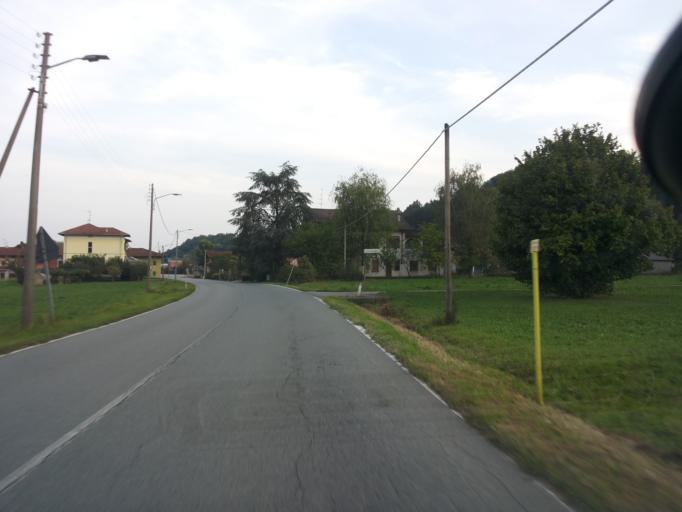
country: IT
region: Piedmont
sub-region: Provincia di Biella
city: Mottalciata
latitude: 45.5180
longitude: 8.2002
